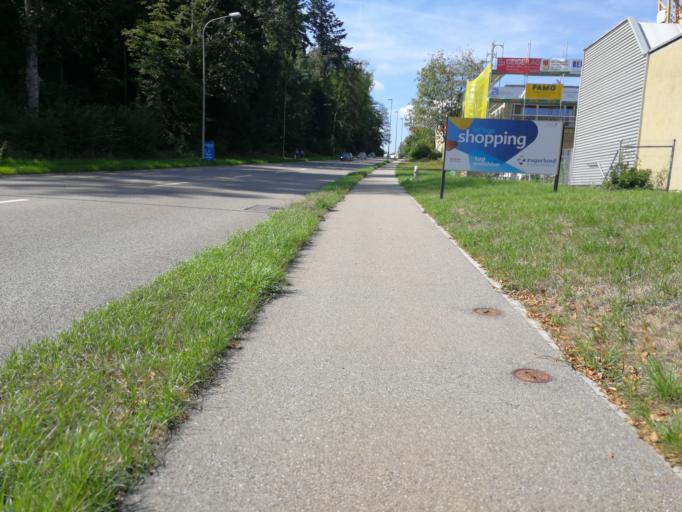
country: CH
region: Zurich
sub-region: Bezirk Horgen
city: Au
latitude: 47.2372
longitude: 8.6454
